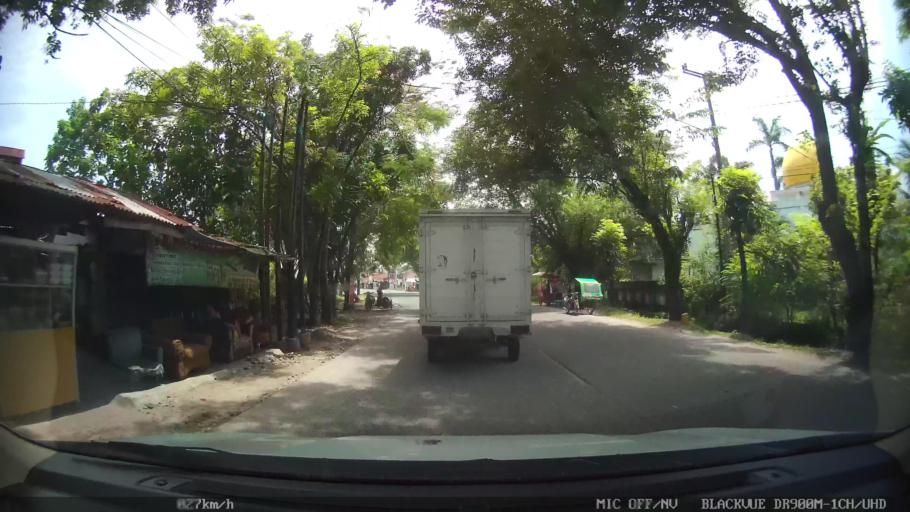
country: ID
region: North Sumatra
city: Sunggal
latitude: 3.5815
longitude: 98.6395
